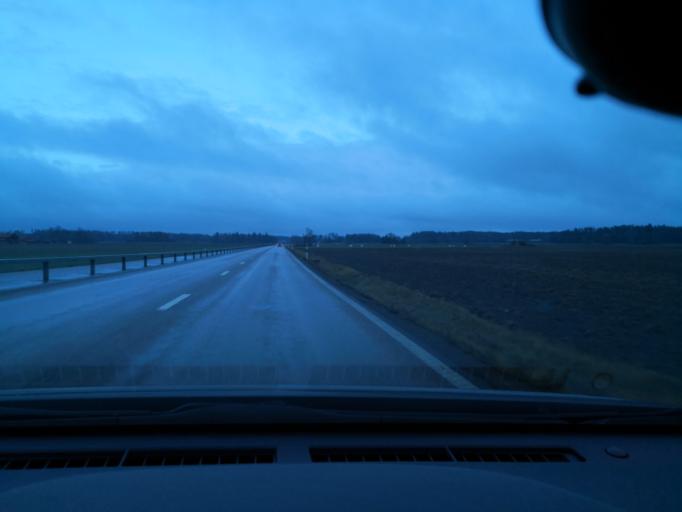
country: SE
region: Vaestmanland
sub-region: Vasteras
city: Skultuna
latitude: 59.5782
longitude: 16.4042
